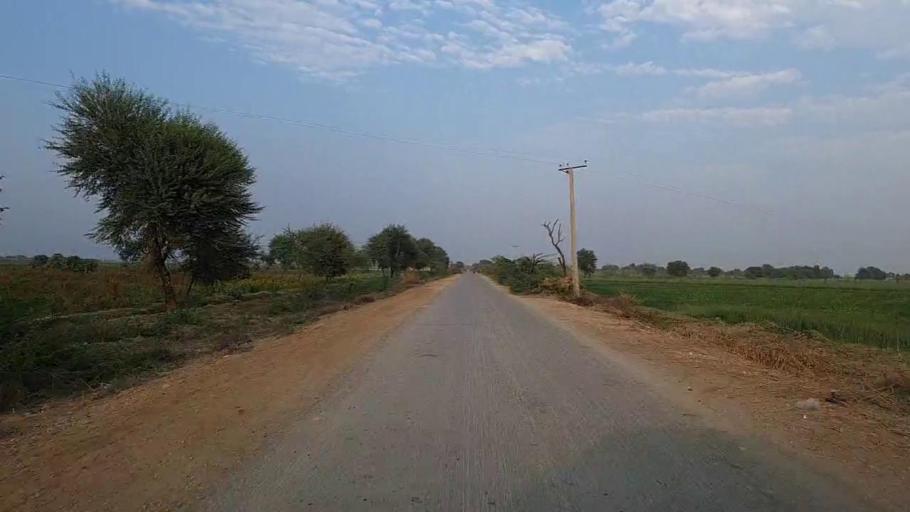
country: PK
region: Sindh
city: Samaro
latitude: 25.3956
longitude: 69.3762
